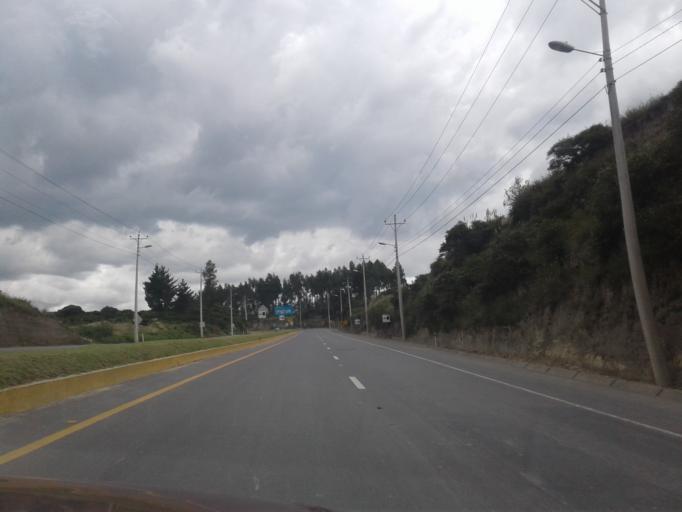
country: EC
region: Pichincha
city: Sangolqui
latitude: -0.3057
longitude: -78.3627
